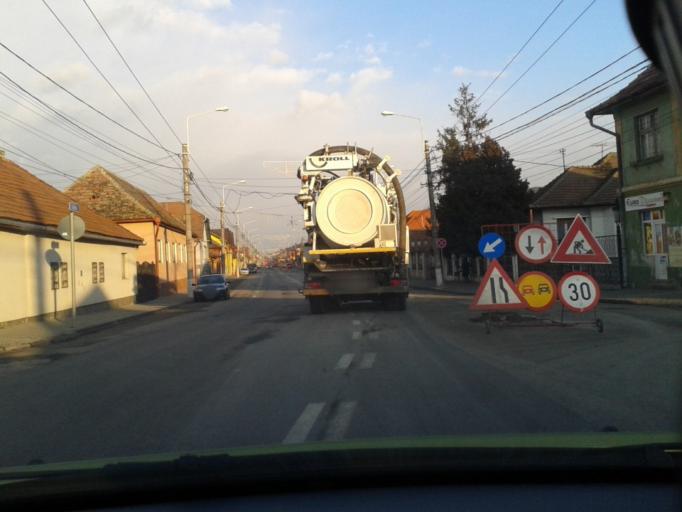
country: RO
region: Sibiu
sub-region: Municipiul Medias
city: Medias
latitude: 46.1656
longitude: 24.3603
